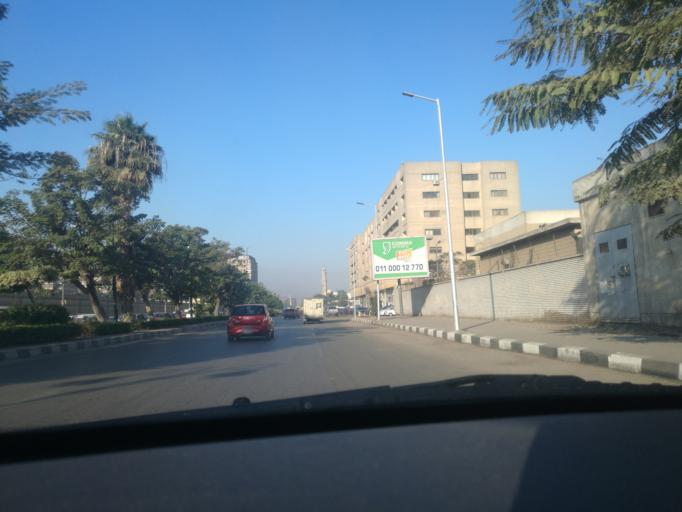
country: EG
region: Muhafazat al Qahirah
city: Cairo
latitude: 30.1023
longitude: 31.3043
